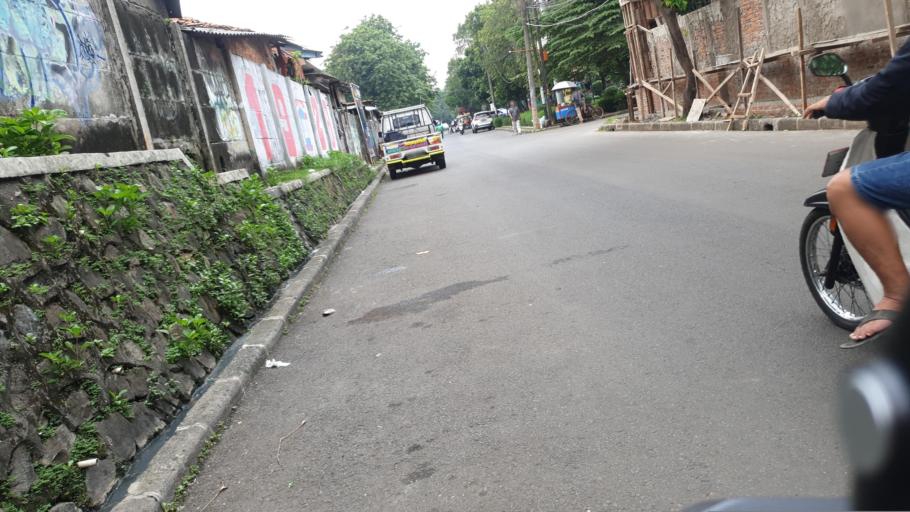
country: ID
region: West Java
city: Ciputat
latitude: -6.1944
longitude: 106.7510
